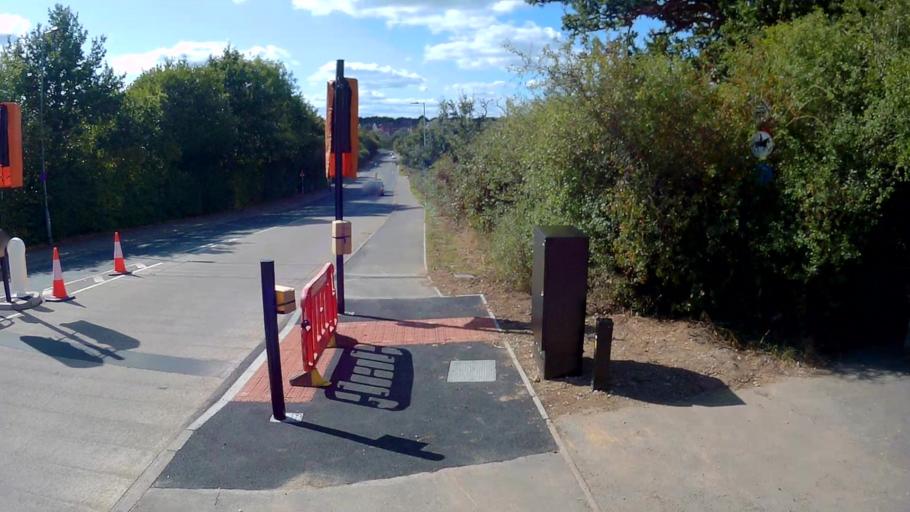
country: GB
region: England
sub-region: Bracknell Forest
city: Bracknell
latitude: 51.4295
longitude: -0.7510
